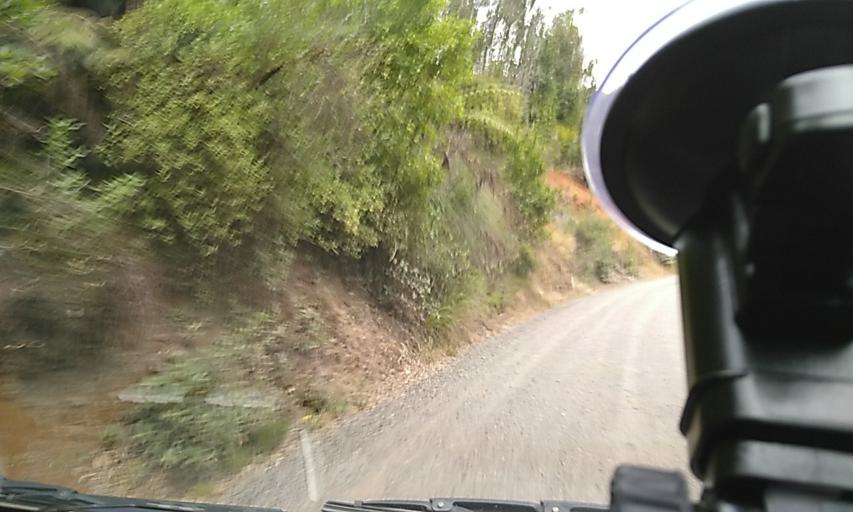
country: NZ
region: Northland
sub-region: Kaipara District
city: Dargaville
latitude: -35.6528
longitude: 173.5681
